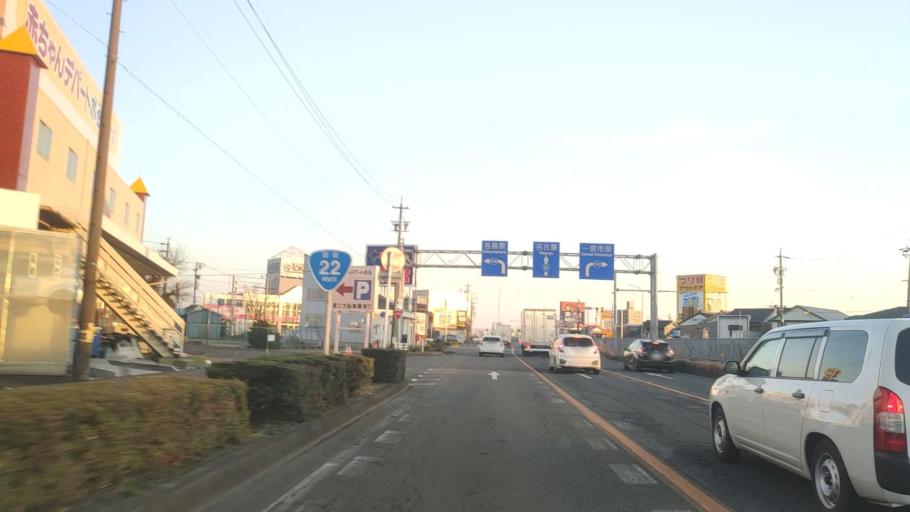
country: JP
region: Aichi
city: Ichinomiya
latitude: 35.3221
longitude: 136.8093
